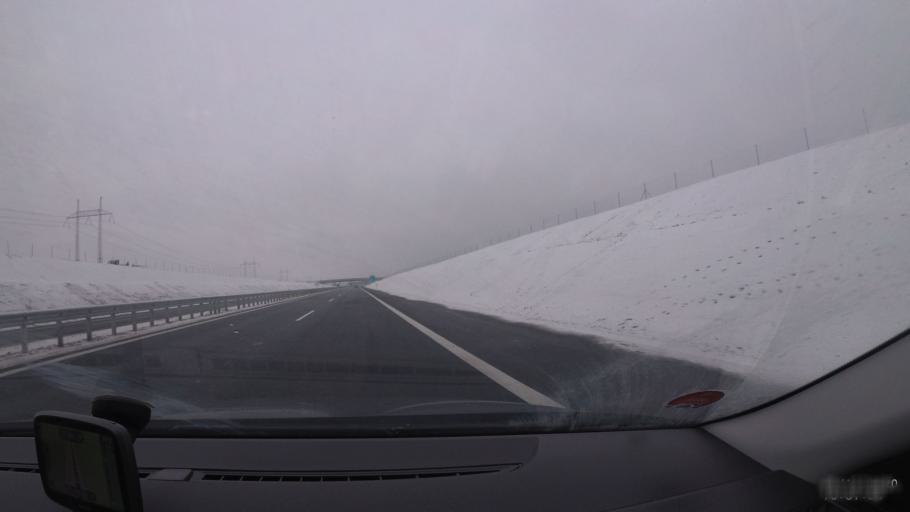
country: CZ
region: Central Bohemia
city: Revnicov
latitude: 50.1774
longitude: 13.8004
